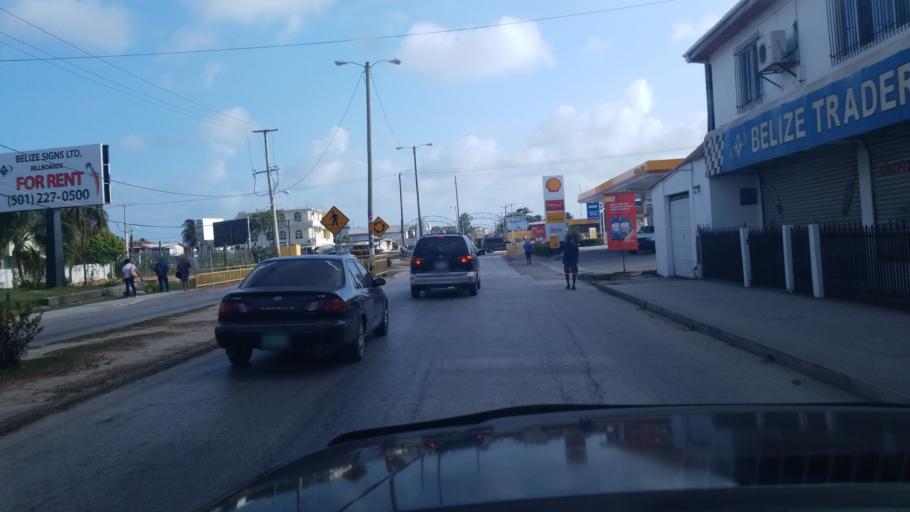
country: BZ
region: Belize
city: Belize City
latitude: 17.4947
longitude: -88.1990
